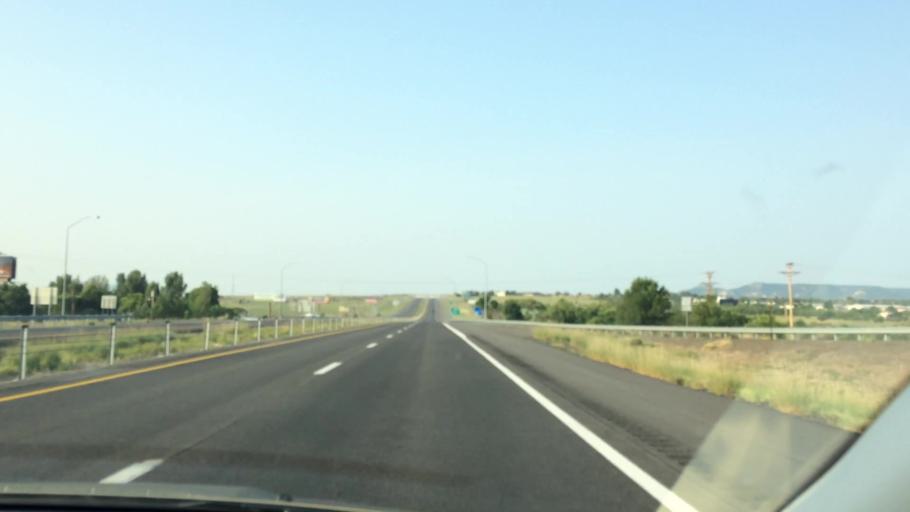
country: US
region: New Mexico
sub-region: Colfax County
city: Raton
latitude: 36.8838
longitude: -104.4317
